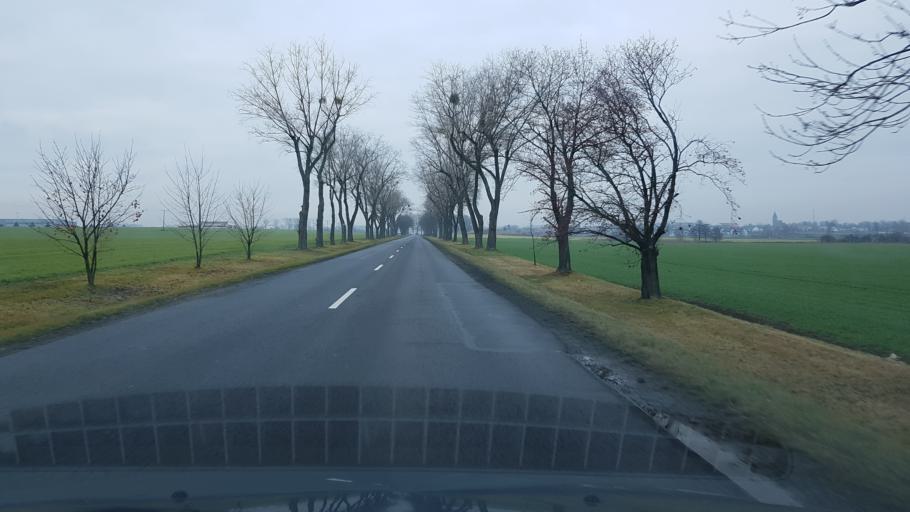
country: PL
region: Lower Silesian Voivodeship
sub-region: Powiat wroclawski
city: Bielany Wroclawskie
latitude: 51.0001
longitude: 16.9714
